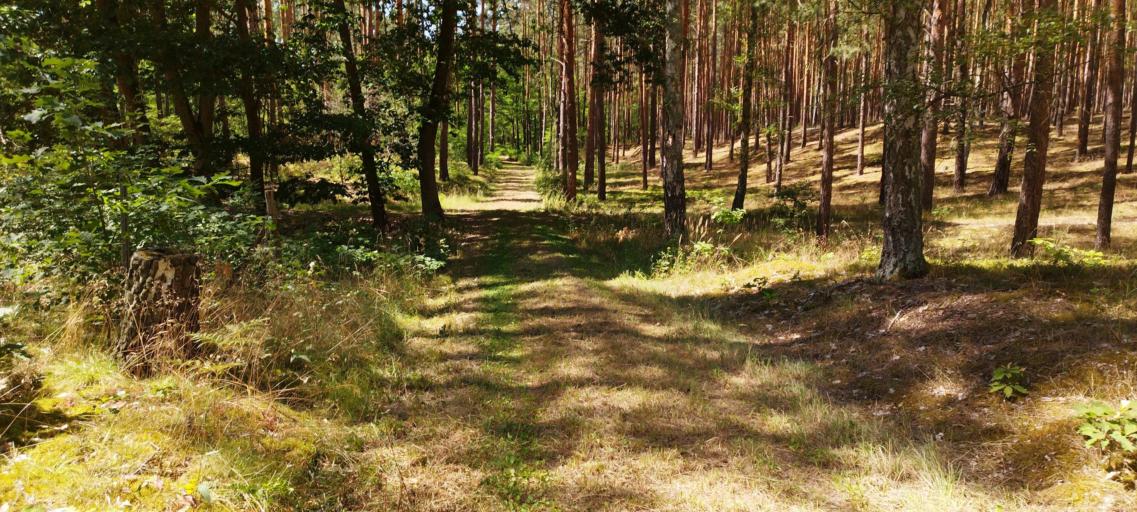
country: DE
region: Brandenburg
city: Reichenwalde
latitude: 52.2778
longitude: 13.9793
